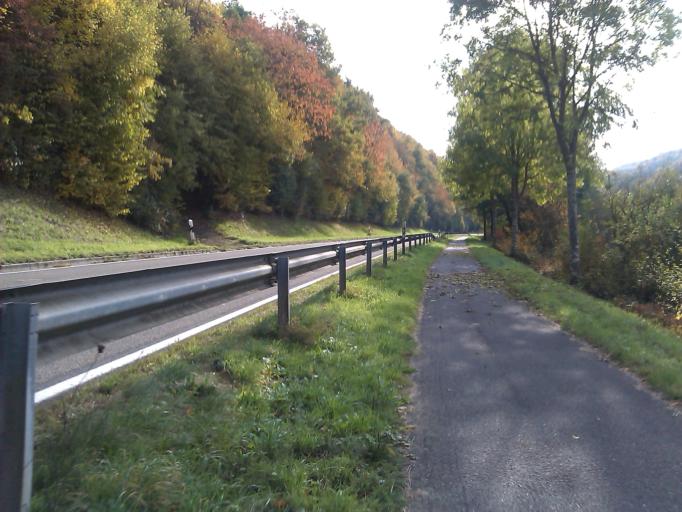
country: DE
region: Rheinland-Pfalz
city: Adenbach
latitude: 49.6727
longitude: 7.6511
